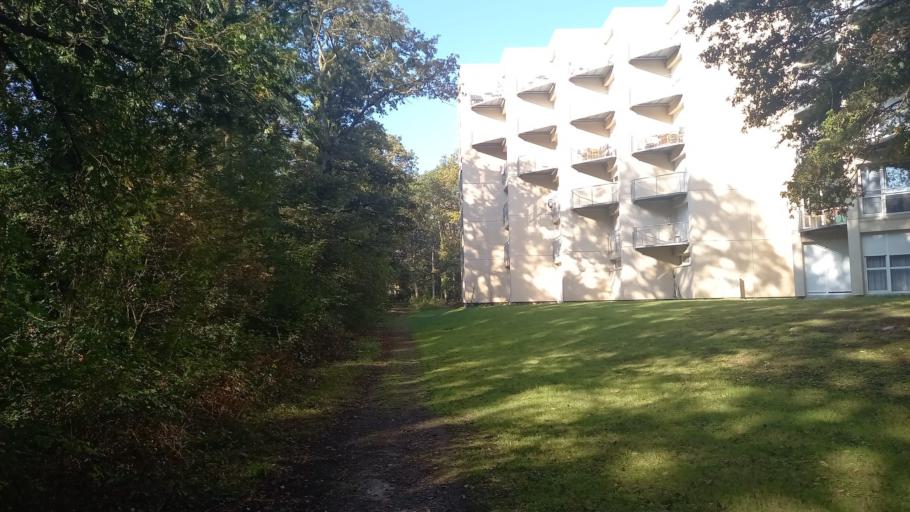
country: FR
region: Centre
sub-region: Departement d'Indre-et-Loire
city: Chambray-les-Tours
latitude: 47.3538
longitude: 0.7018
